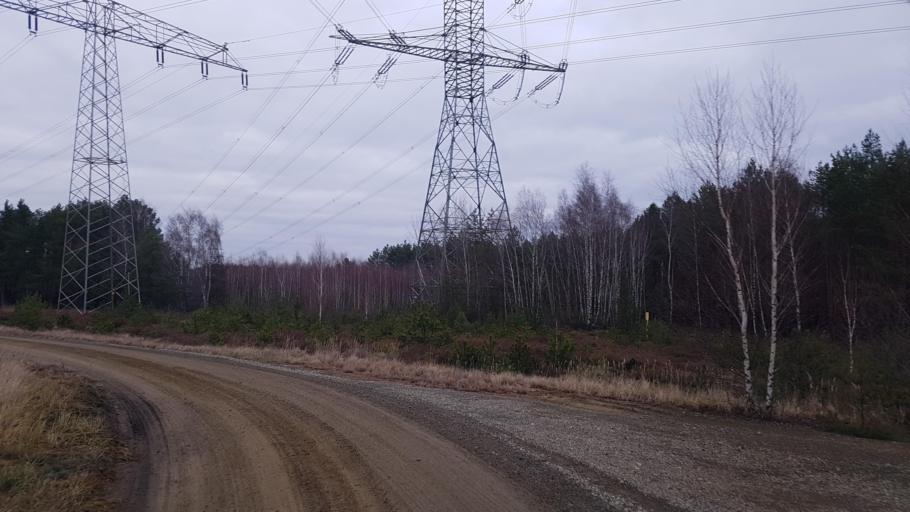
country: DE
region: Brandenburg
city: Altdobern
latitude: 51.6414
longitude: 14.0053
